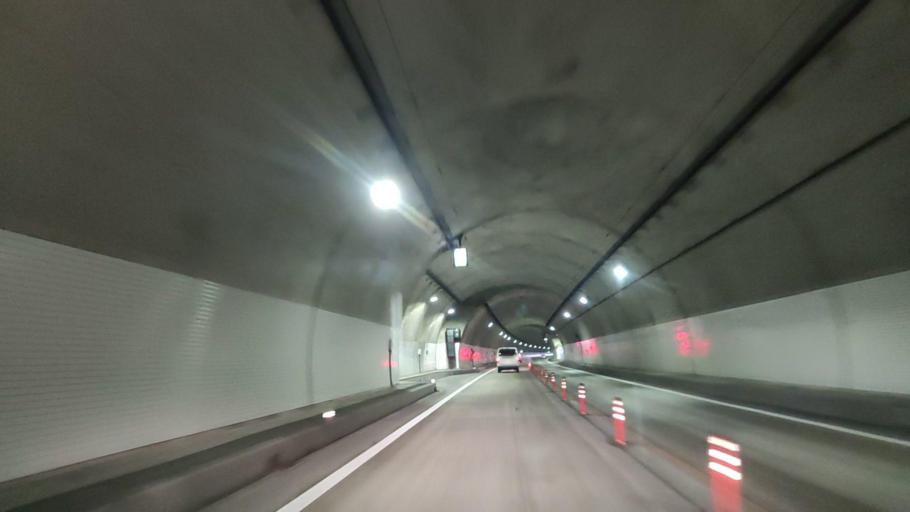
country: JP
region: Akita
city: Odate
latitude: 40.3339
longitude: 140.6114
